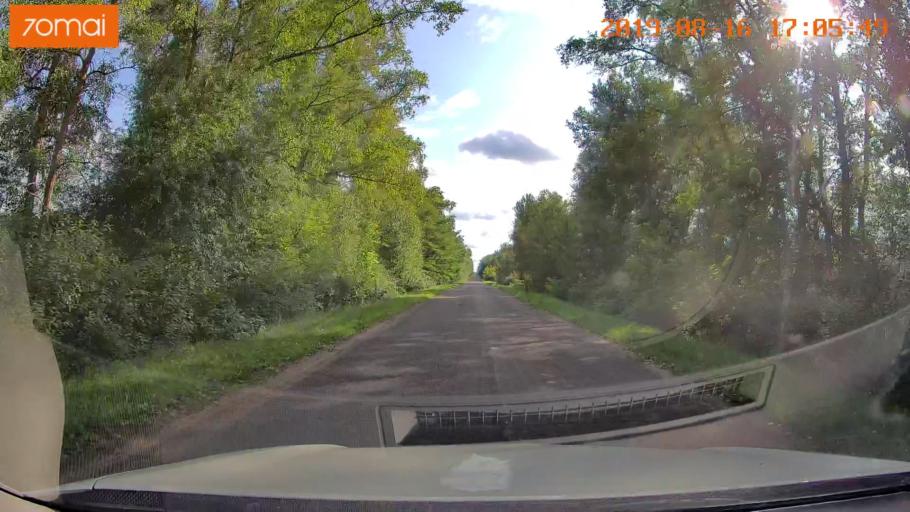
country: BY
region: Mogilev
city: Hlusha
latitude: 53.2337
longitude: 28.9402
